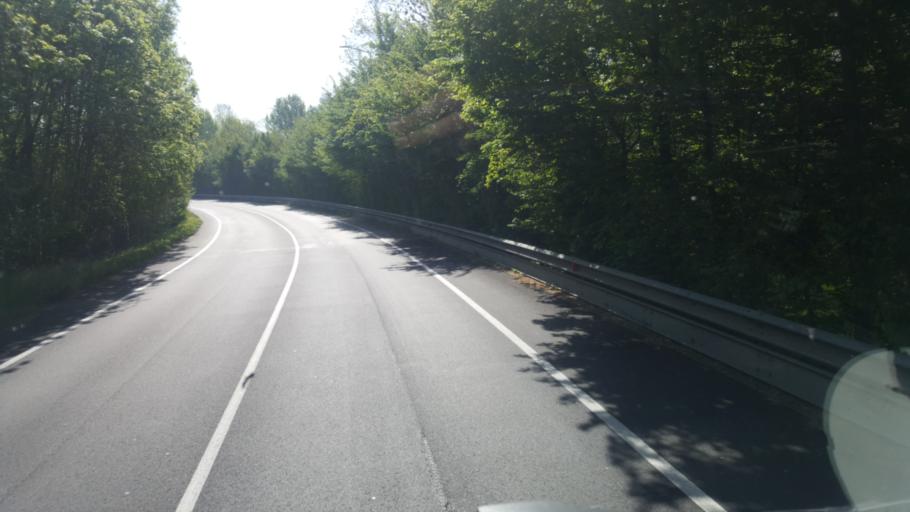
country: IT
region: Lombardy
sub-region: Provincia di Varese
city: Bodio
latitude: 45.8117
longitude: 8.7647
